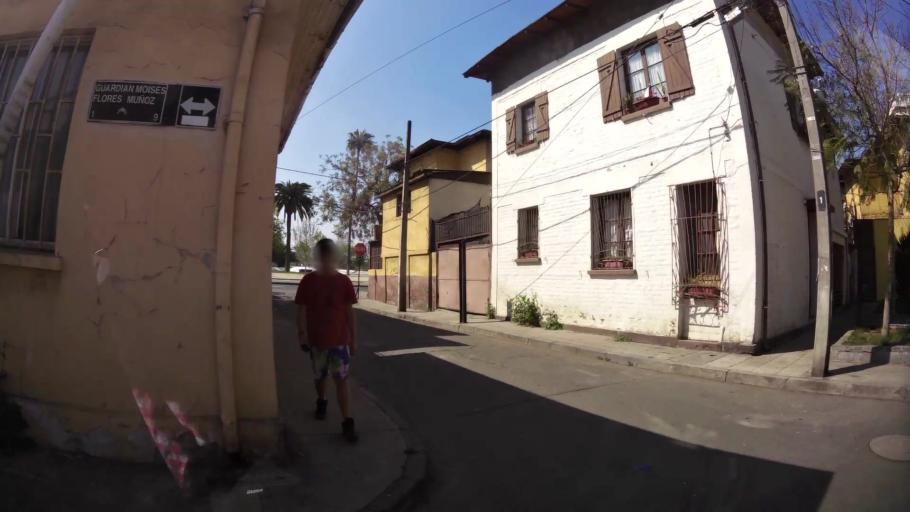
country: CL
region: Santiago Metropolitan
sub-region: Provincia de Santiago
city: Santiago
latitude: -33.4289
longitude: -70.6708
